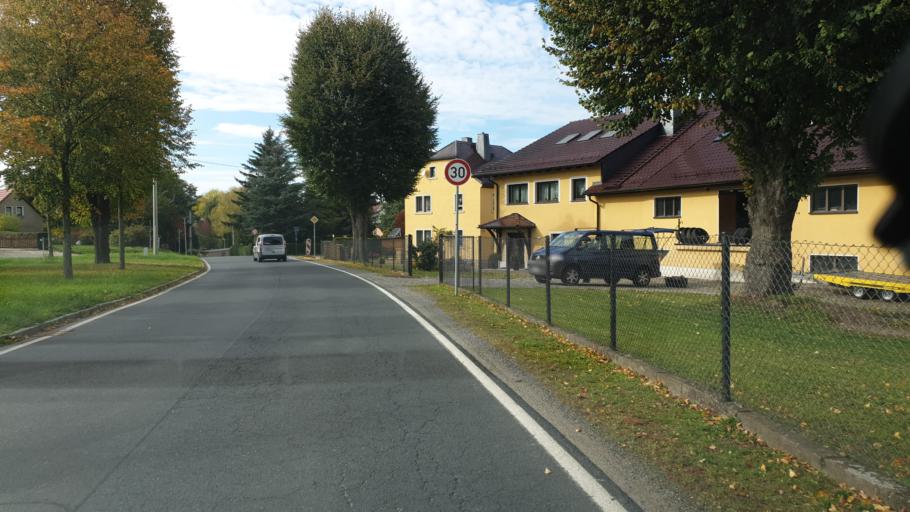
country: DE
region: Saxony
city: Durrrohrsdorf
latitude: 51.0405
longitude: 13.9265
